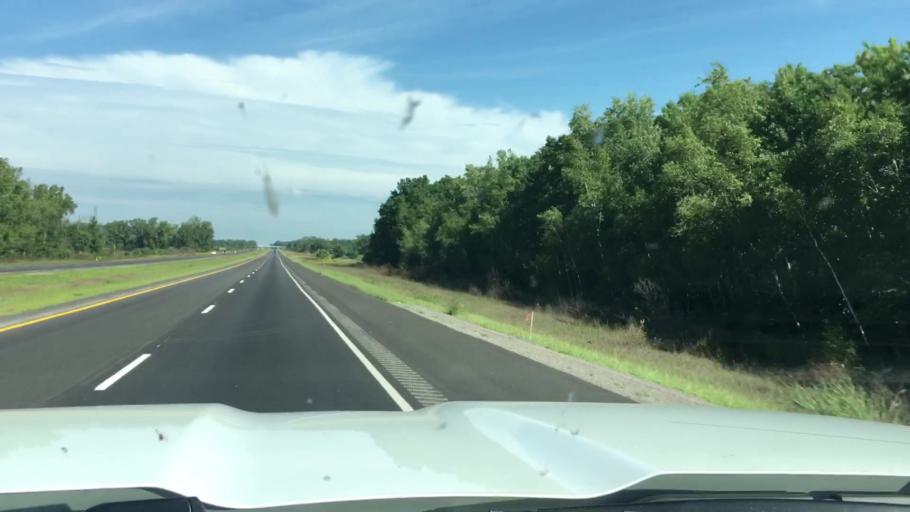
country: US
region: Michigan
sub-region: Saginaw County
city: Freeland
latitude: 43.5482
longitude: -84.1387
